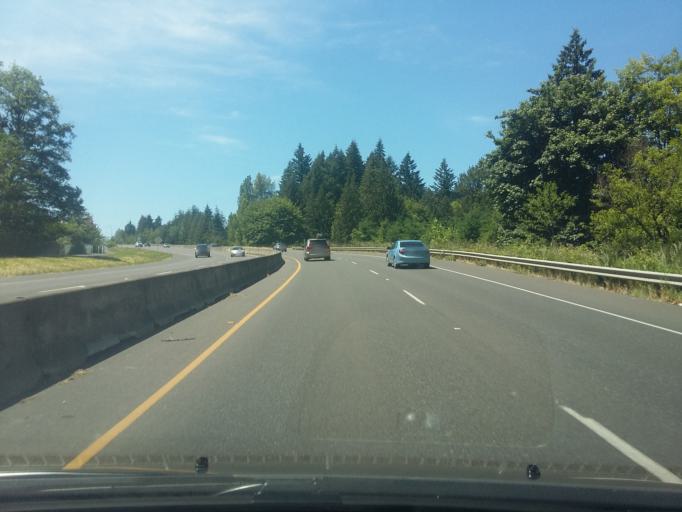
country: US
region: Washington
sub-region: Clark County
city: Five Corners
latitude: 45.6834
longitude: -122.5861
